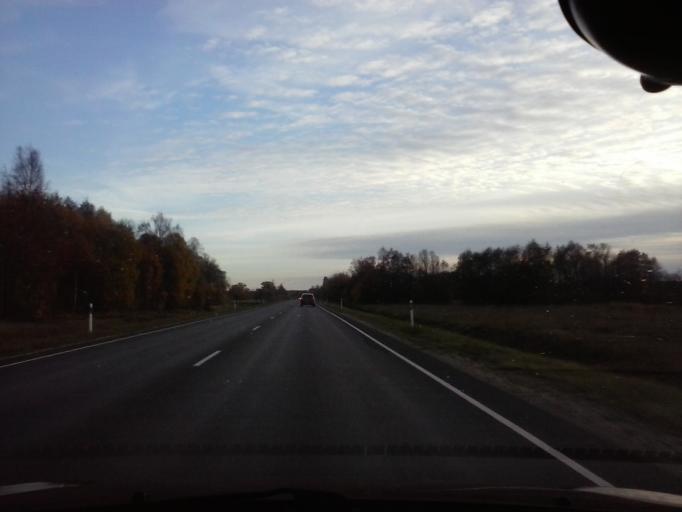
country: EE
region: Harju
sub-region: Nissi vald
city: Turba
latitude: 58.9150
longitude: 24.1119
